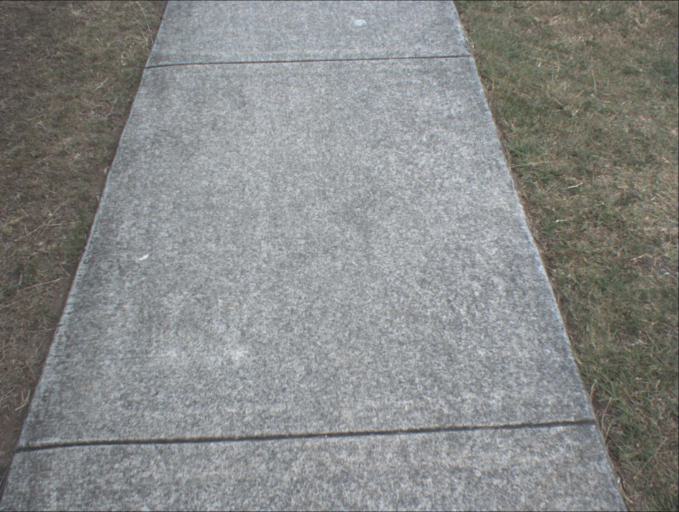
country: AU
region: Queensland
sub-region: Logan
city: Slacks Creek
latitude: -27.6766
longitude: 153.1758
